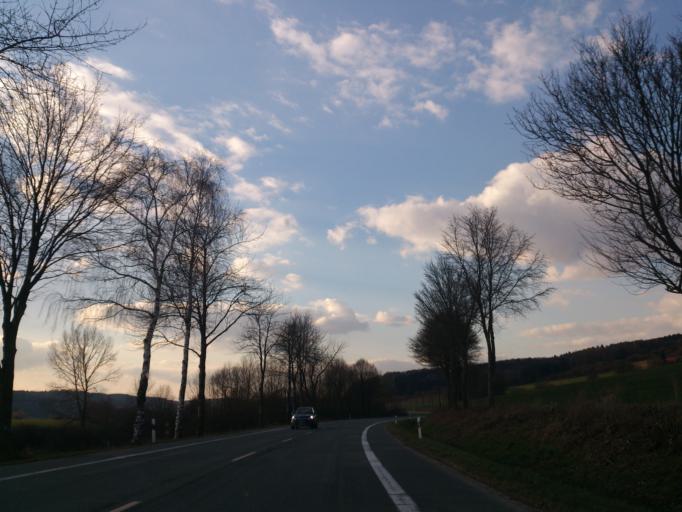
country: DE
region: North Rhine-Westphalia
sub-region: Regierungsbezirk Detmold
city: Willebadessen
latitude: 51.6389
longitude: 9.0208
